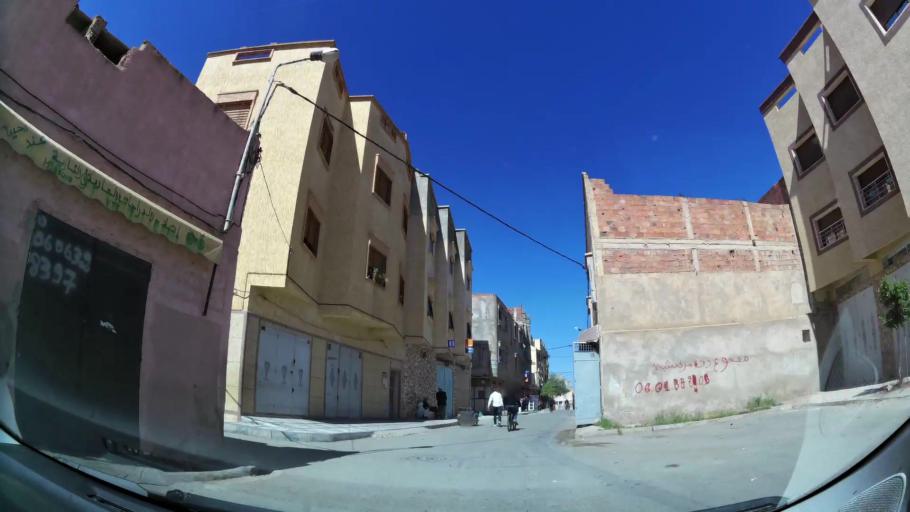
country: MA
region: Oriental
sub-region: Oujda-Angad
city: Oujda
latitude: 34.6611
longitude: -1.8903
